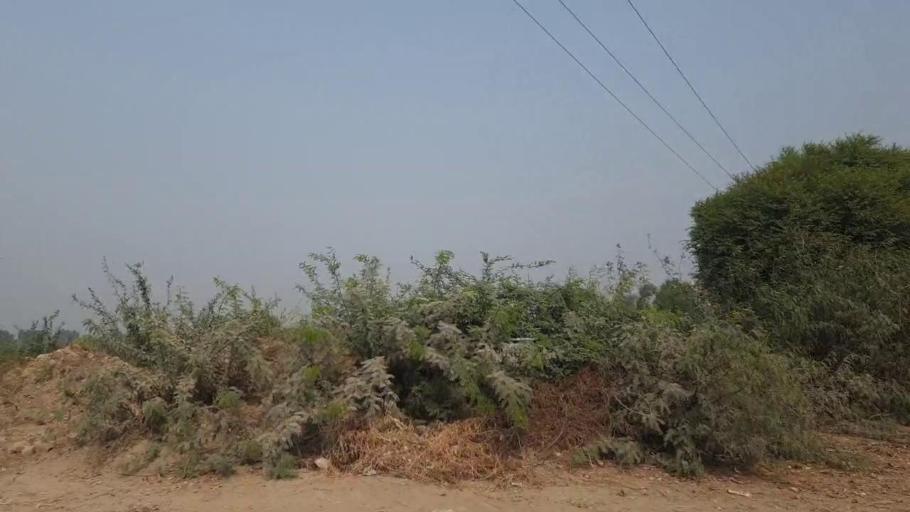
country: PK
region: Sindh
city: Tando Muhammad Khan
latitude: 25.1810
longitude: 68.5985
